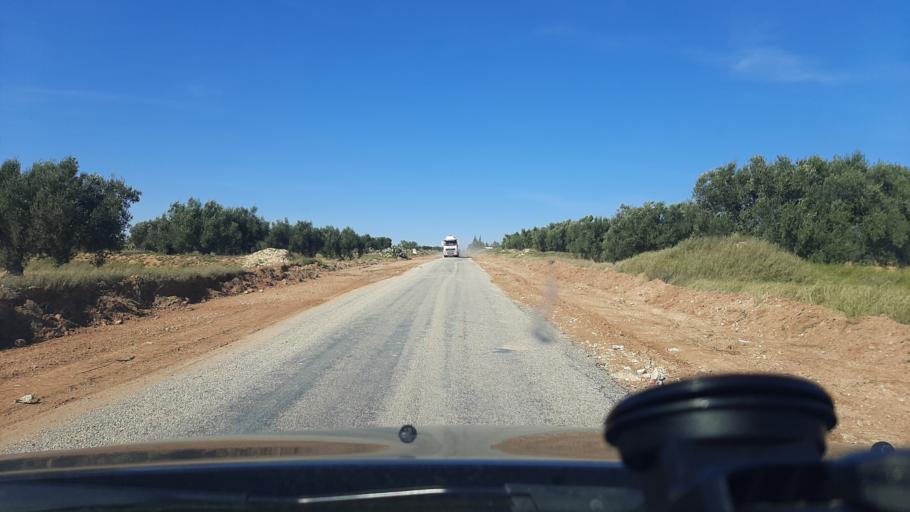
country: TN
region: Safaqis
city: Sfax
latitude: 34.9377
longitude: 10.5611
